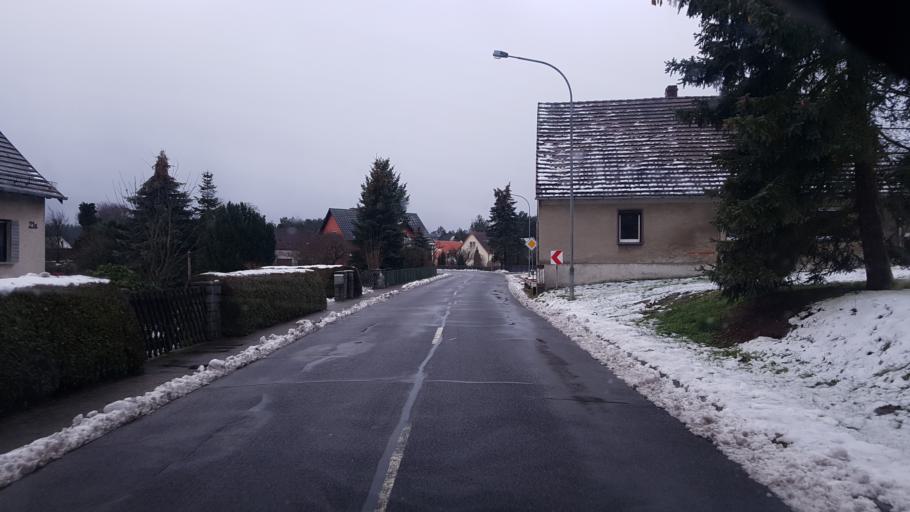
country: DE
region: Brandenburg
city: Schenkendobern
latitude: 51.9331
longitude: 14.6215
